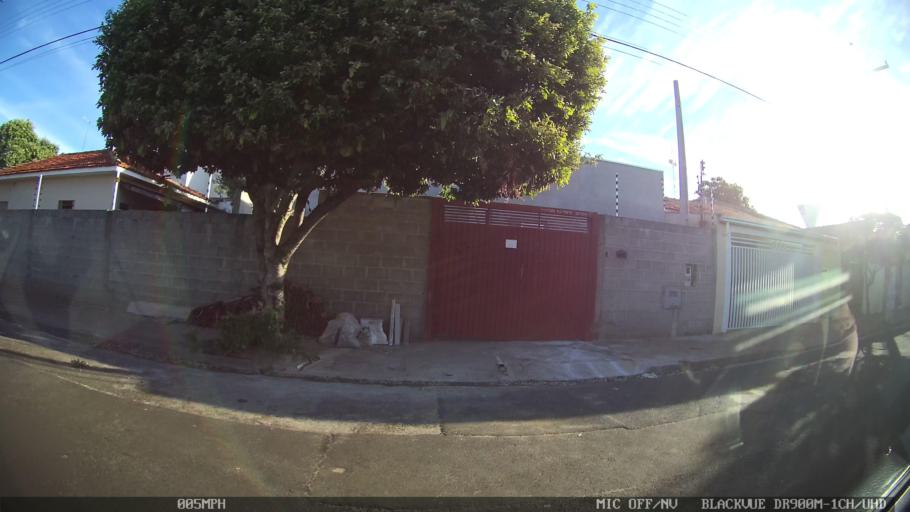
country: BR
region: Sao Paulo
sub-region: Sao Jose Do Rio Preto
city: Sao Jose do Rio Preto
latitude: -20.8304
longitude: -49.3709
